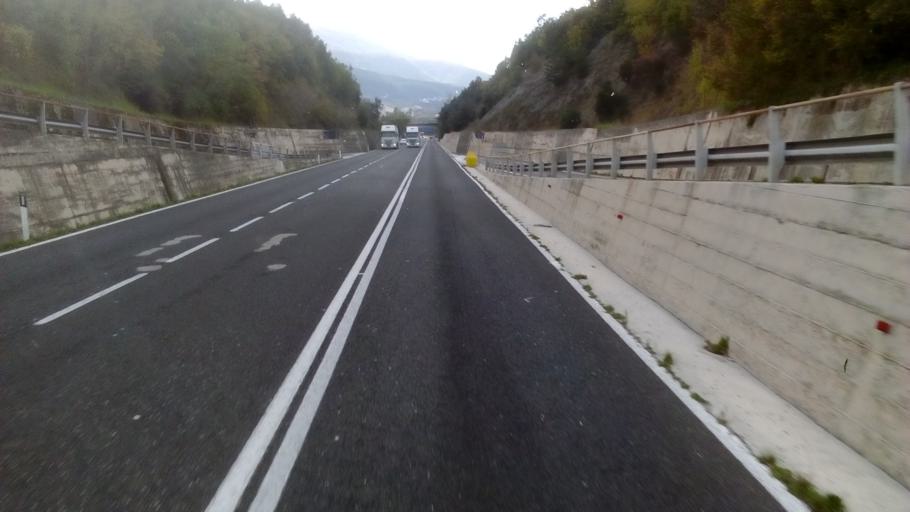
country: IT
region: Molise
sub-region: Provincia di Isernia
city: Isernia
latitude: 41.5884
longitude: 14.2384
